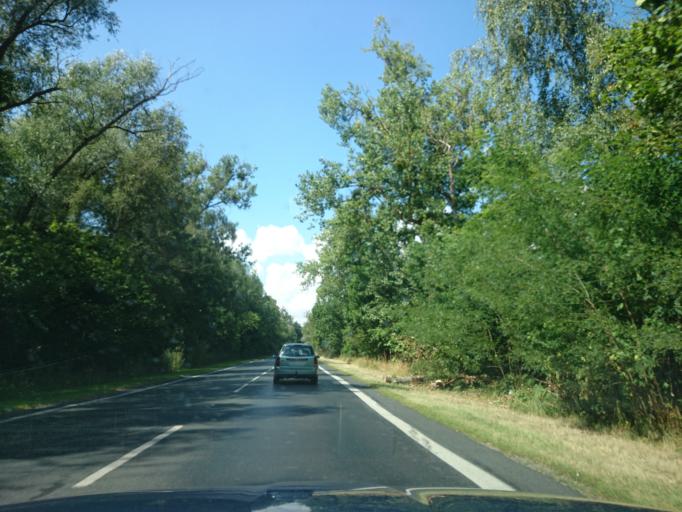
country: PL
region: West Pomeranian Voivodeship
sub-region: Szczecin
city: Szczecin
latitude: 53.3746
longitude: 14.5699
